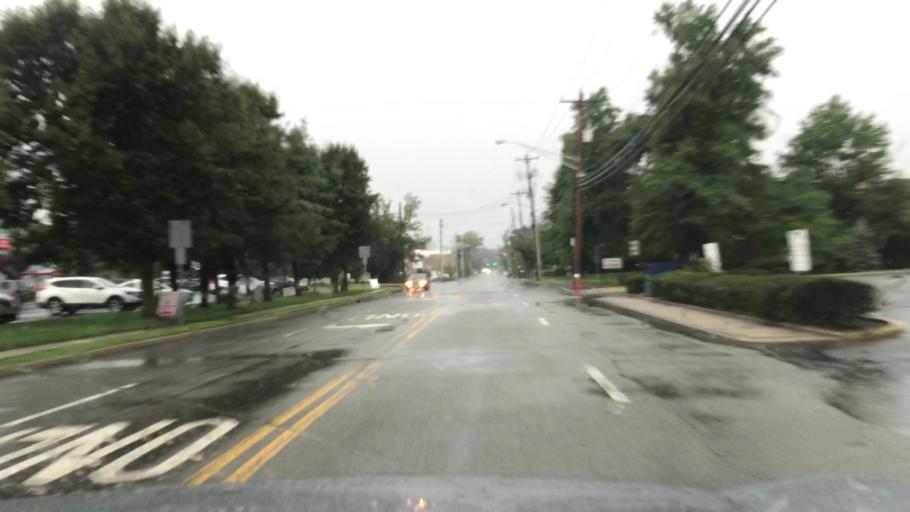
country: US
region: New Jersey
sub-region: Bergen County
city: Closter
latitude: 40.9694
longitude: -73.9529
